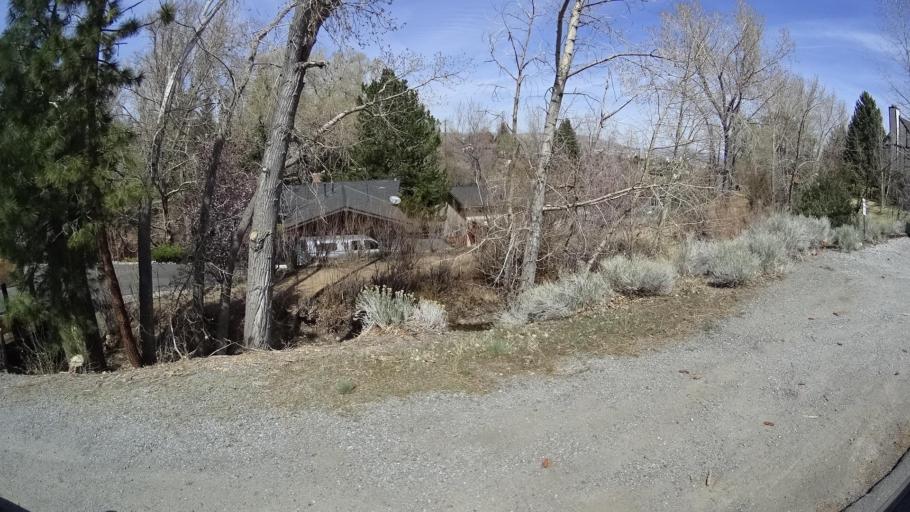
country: US
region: Nevada
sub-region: Washoe County
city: Reno
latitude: 39.4912
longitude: -119.8418
